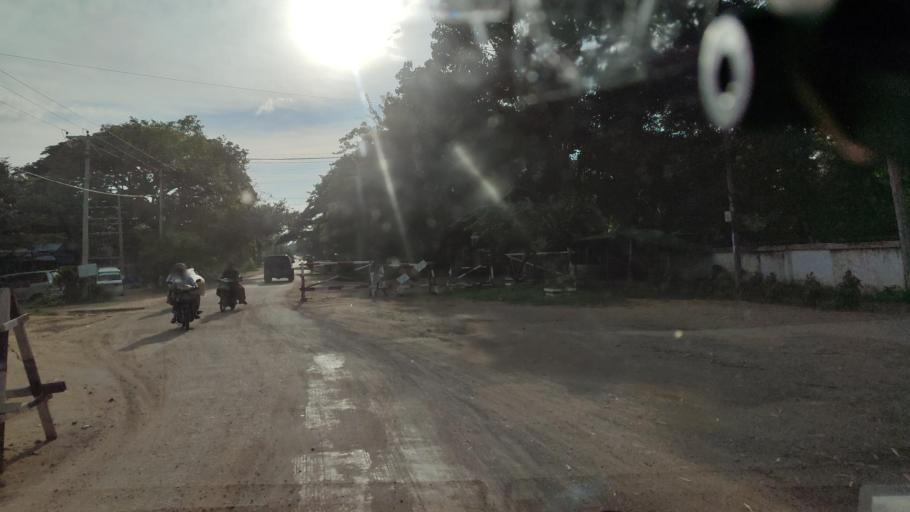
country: MM
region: Magway
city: Chauk
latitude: 20.8337
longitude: 95.1189
